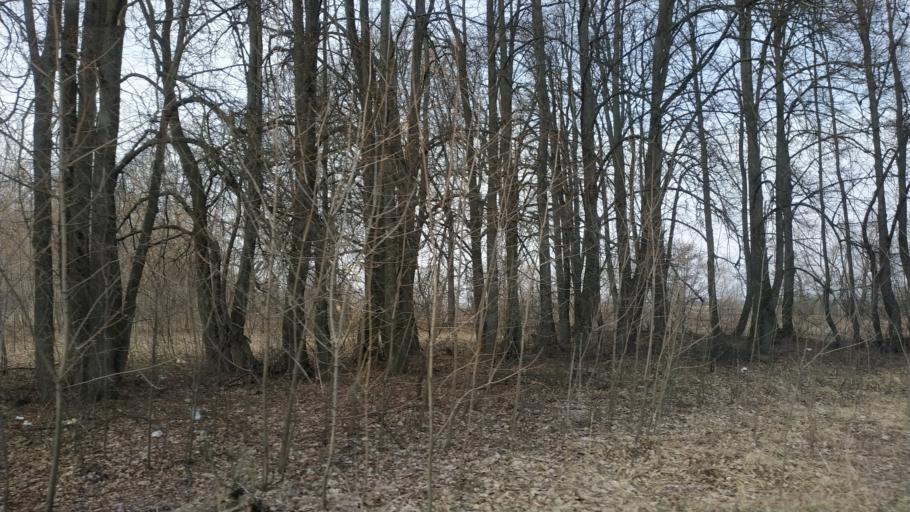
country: RU
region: Moskovskaya
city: Malyshevo
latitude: 55.4006
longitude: 38.3607
